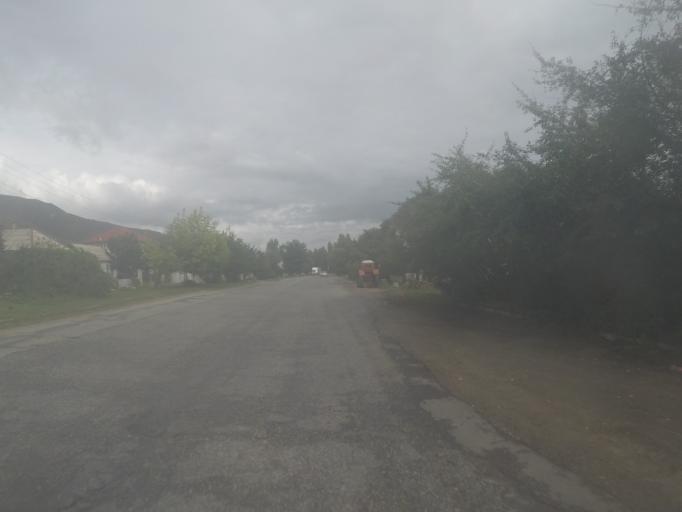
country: KG
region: Ysyk-Koel
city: Tyup
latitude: 42.7421
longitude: 78.0231
